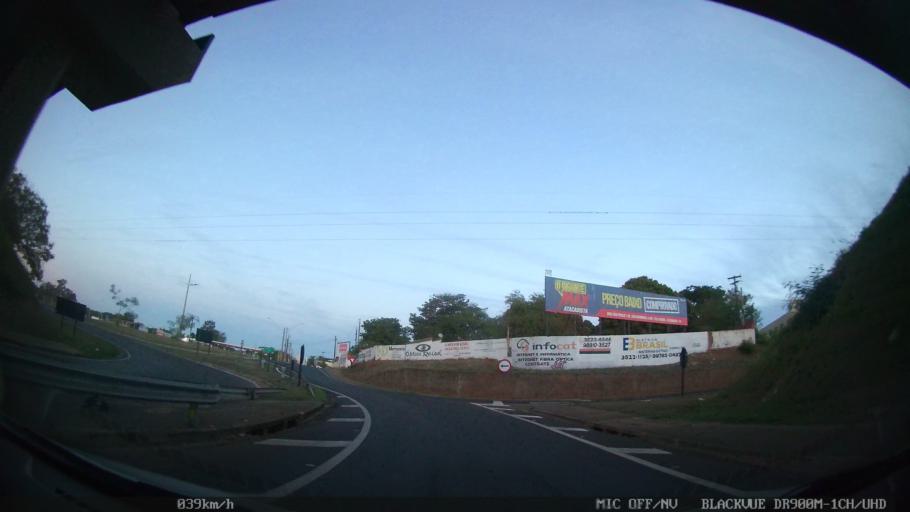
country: BR
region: Sao Paulo
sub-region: Catanduva
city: Catanduva
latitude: -21.1213
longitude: -48.9906
